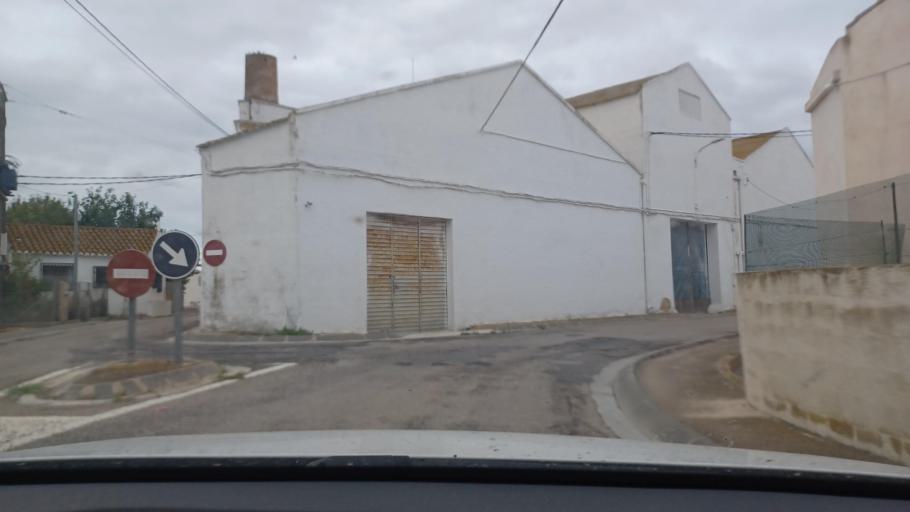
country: ES
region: Catalonia
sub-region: Provincia de Tarragona
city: Deltebre
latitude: 40.7246
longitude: 0.6812
